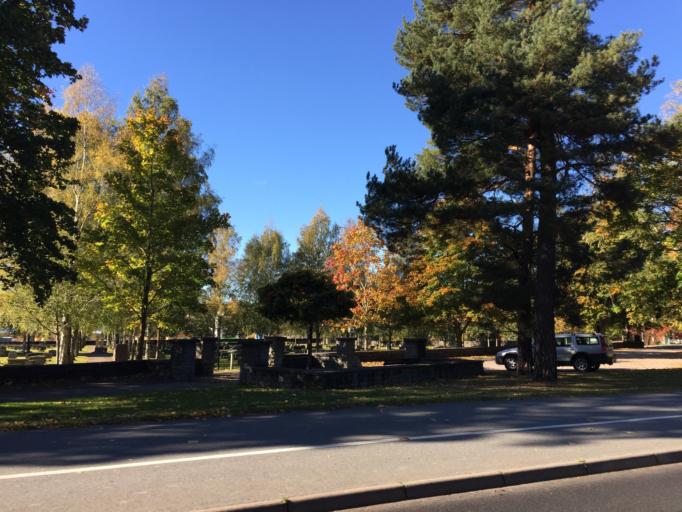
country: SE
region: OErebro
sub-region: Kumla Kommun
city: Kumla
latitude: 59.1216
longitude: 15.1538
